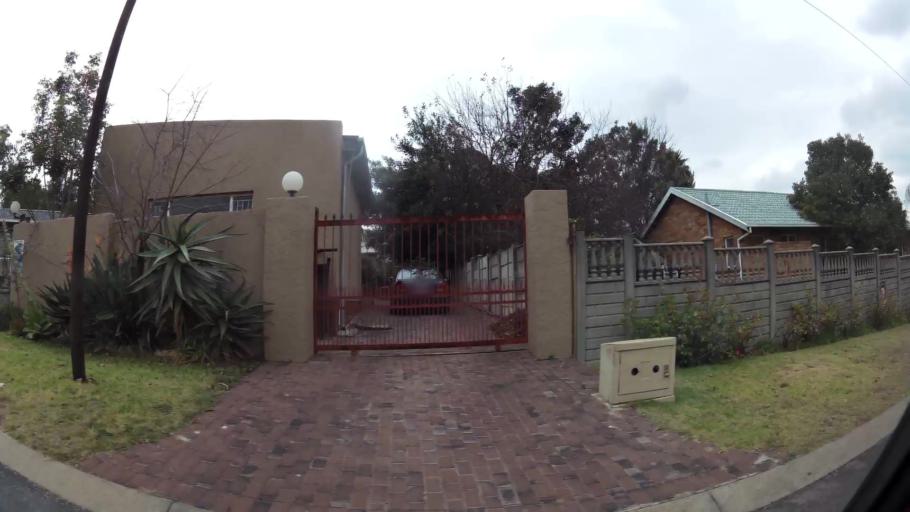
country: ZA
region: Gauteng
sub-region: City of Johannesburg Metropolitan Municipality
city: Roodepoort
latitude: -26.1128
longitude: 27.9063
